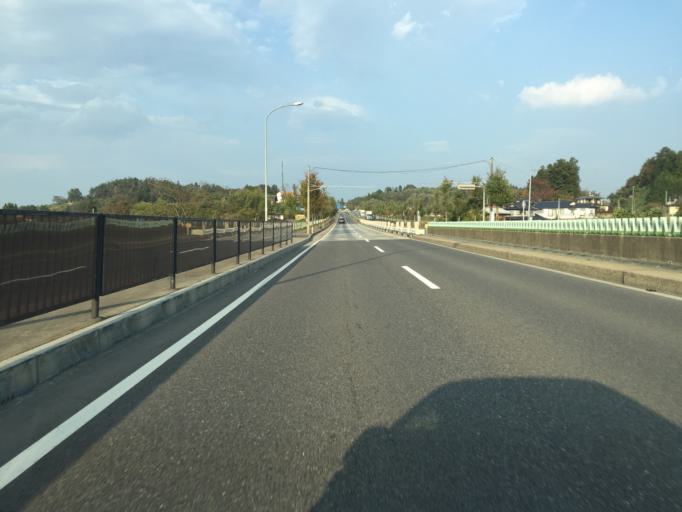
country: JP
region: Fukushima
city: Nihommatsu
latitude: 37.6063
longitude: 140.4672
